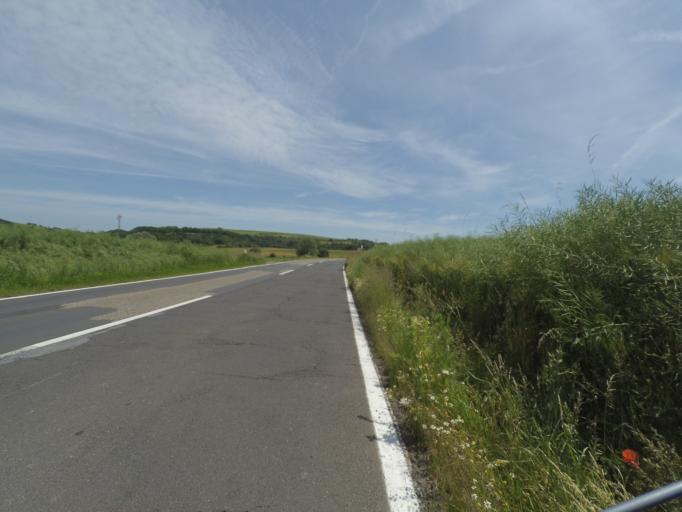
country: DE
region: Rheinland-Pfalz
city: Kerben
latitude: 50.3138
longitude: 7.3557
